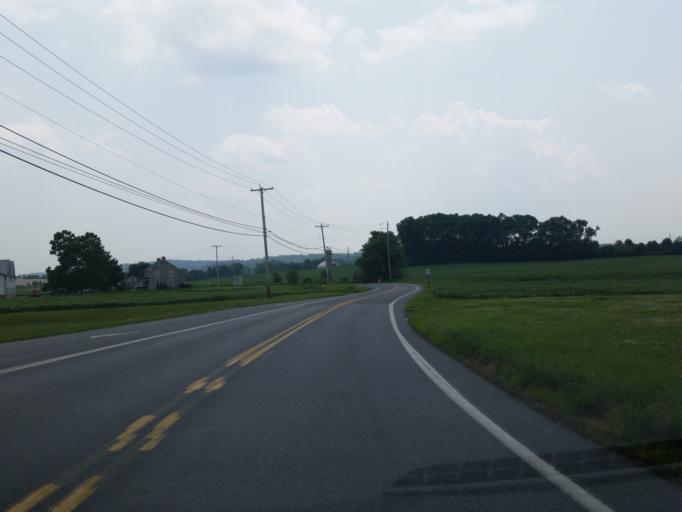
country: US
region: Pennsylvania
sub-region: Lebanon County
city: Campbelltown
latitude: 40.2880
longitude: -76.5979
